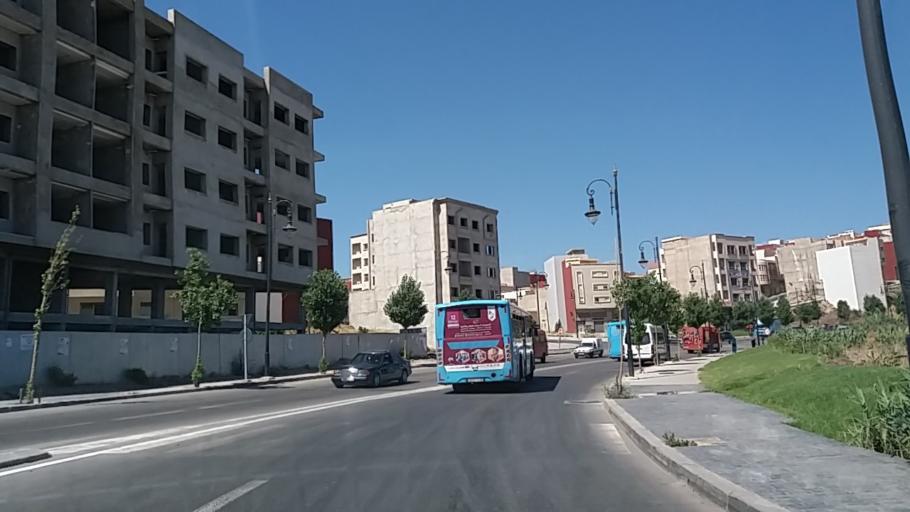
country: MA
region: Tanger-Tetouan
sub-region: Tanger-Assilah
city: Tangier
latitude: 35.7691
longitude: -5.7612
